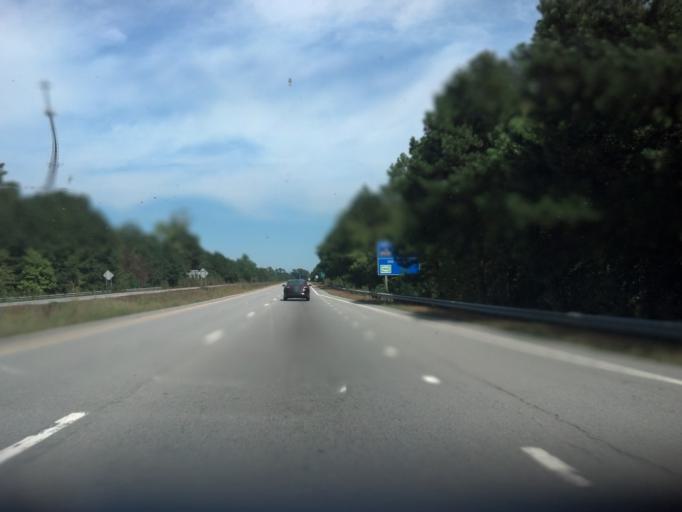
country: US
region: North Carolina
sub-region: Pitt County
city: Summerfield
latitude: 35.6129
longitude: -77.4375
